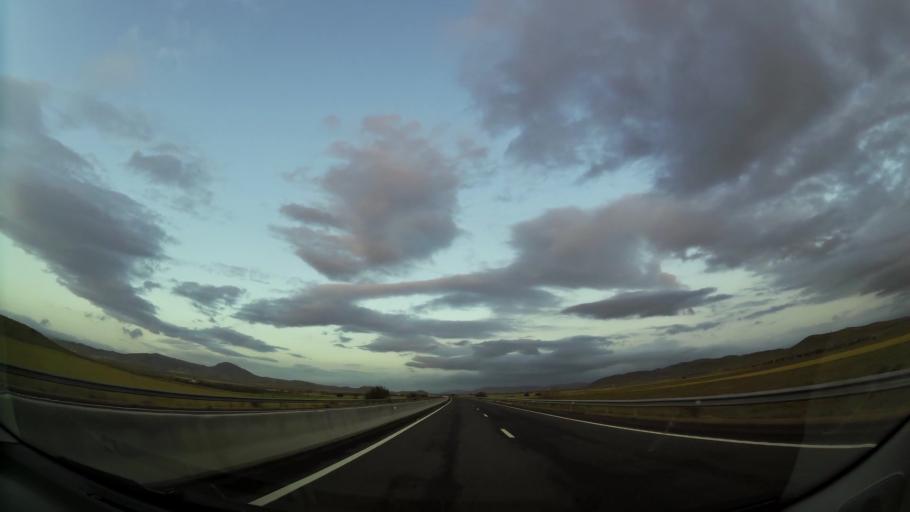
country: MA
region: Oriental
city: El Aioun
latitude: 34.5987
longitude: -2.7298
